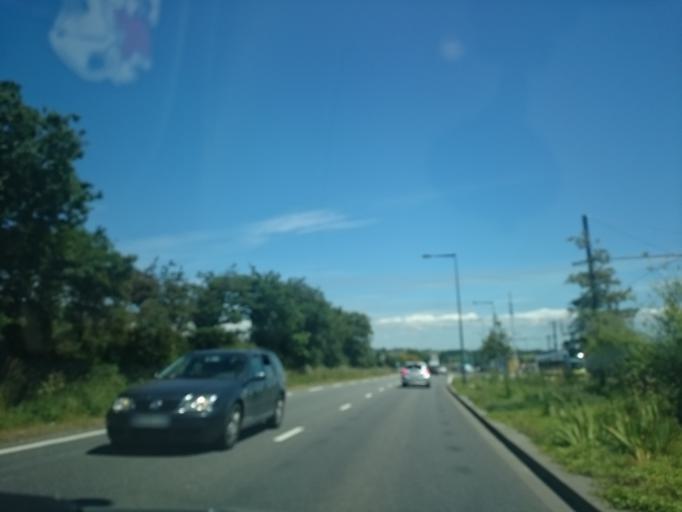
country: FR
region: Brittany
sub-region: Departement du Finistere
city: Gouesnou
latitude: 48.4194
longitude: -4.4453
